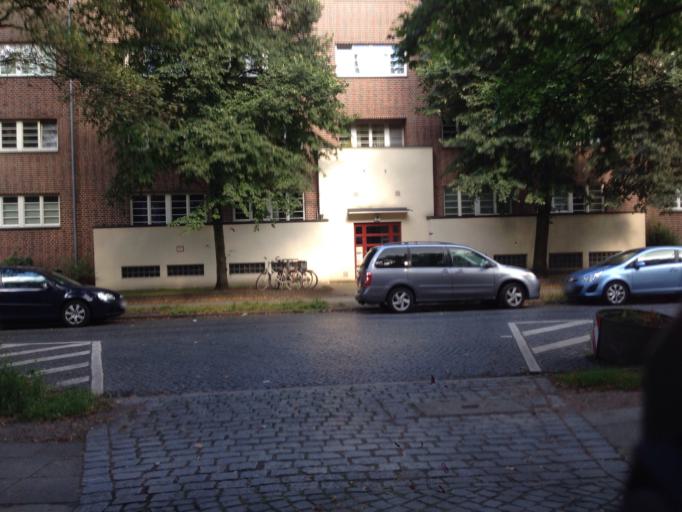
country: DE
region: Hamburg
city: Marienthal
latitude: 53.5825
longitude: 10.0621
